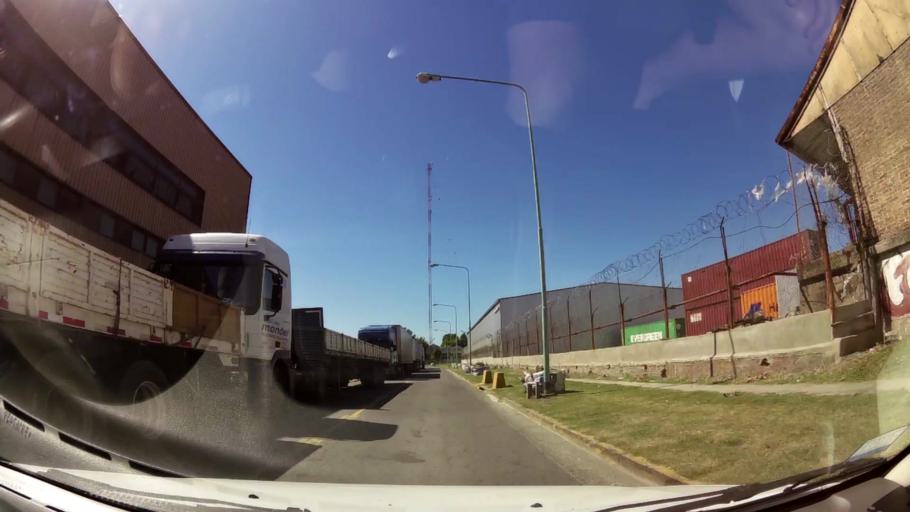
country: AR
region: Buenos Aires F.D.
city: Buenos Aires
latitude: -34.6261
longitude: -58.3522
